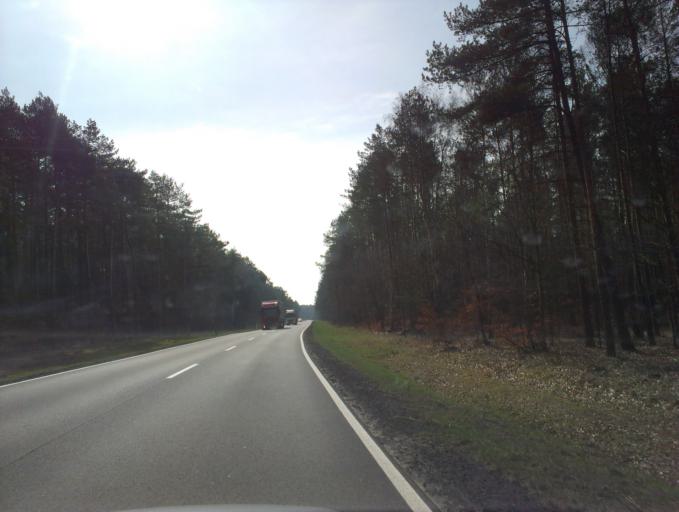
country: PL
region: Greater Poland Voivodeship
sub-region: Powiat zlotowski
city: Tarnowka
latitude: 53.3527
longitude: 16.7883
